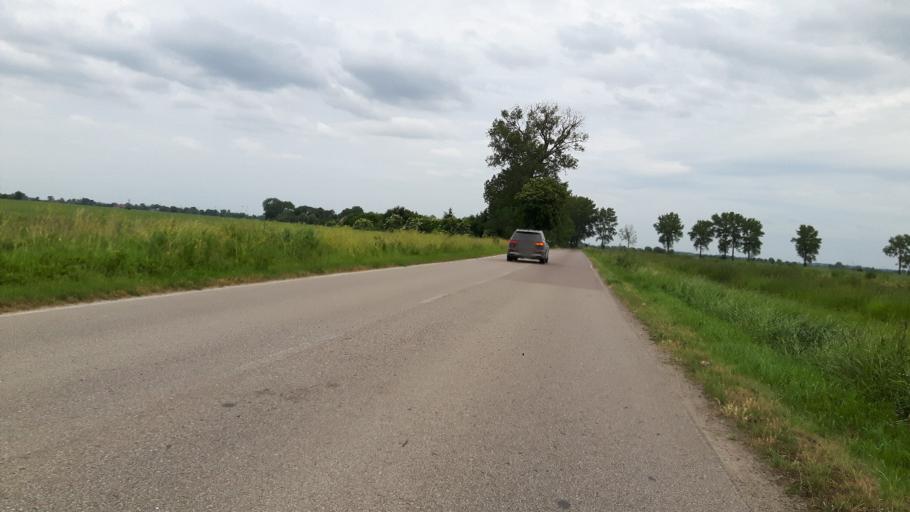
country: PL
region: Pomeranian Voivodeship
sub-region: Powiat nowodworski
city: Sztutowo
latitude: 54.2220
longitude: 19.2590
